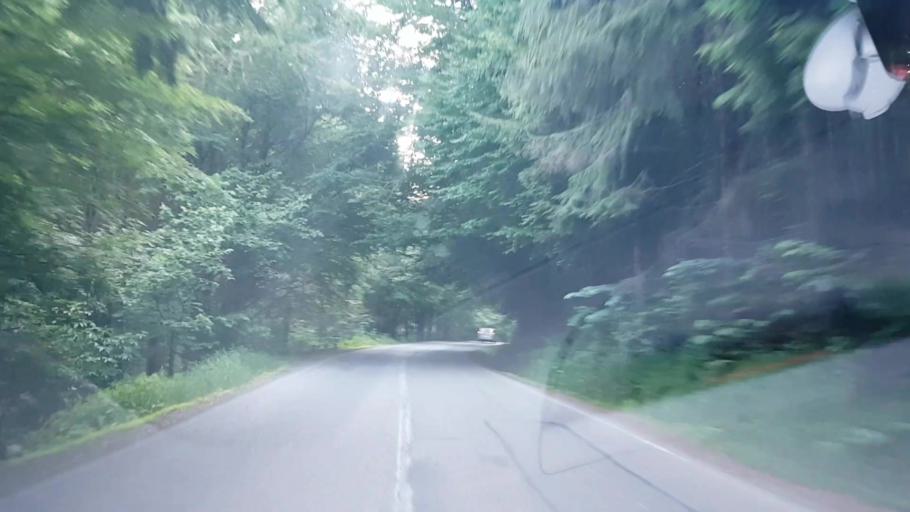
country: RO
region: Harghita
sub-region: Comuna Praid
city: Ocna de Sus
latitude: 46.5812
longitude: 25.2379
